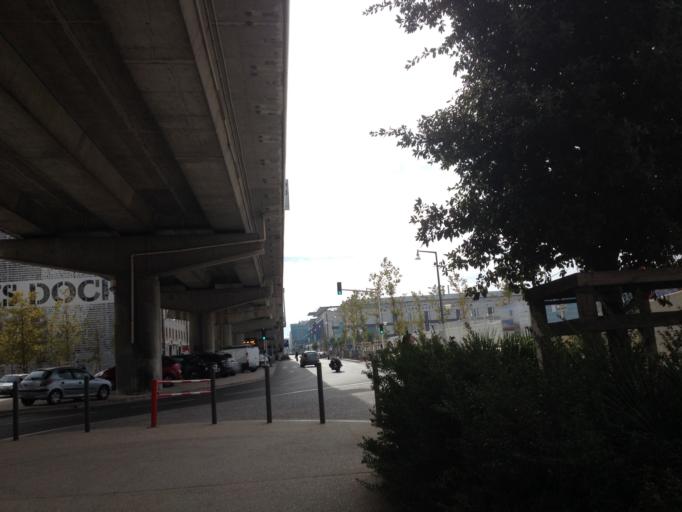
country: FR
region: Provence-Alpes-Cote d'Azur
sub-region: Departement des Bouches-du-Rhone
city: Marseille 03
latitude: 43.3098
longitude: 5.3667
